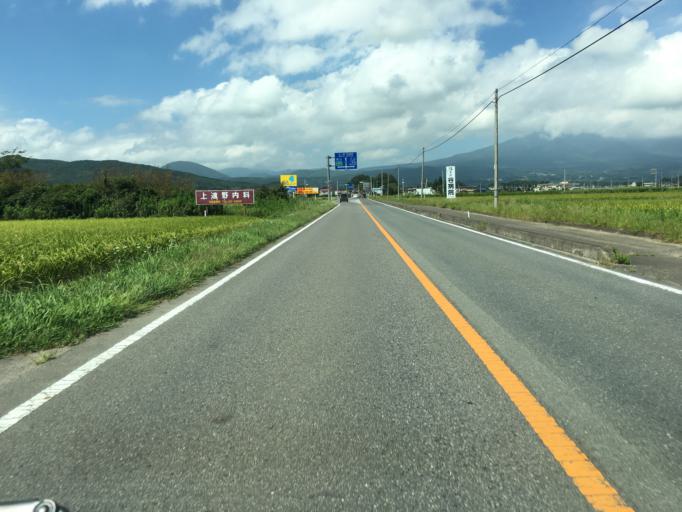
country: JP
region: Fukushima
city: Motomiya
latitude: 37.5261
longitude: 140.3784
